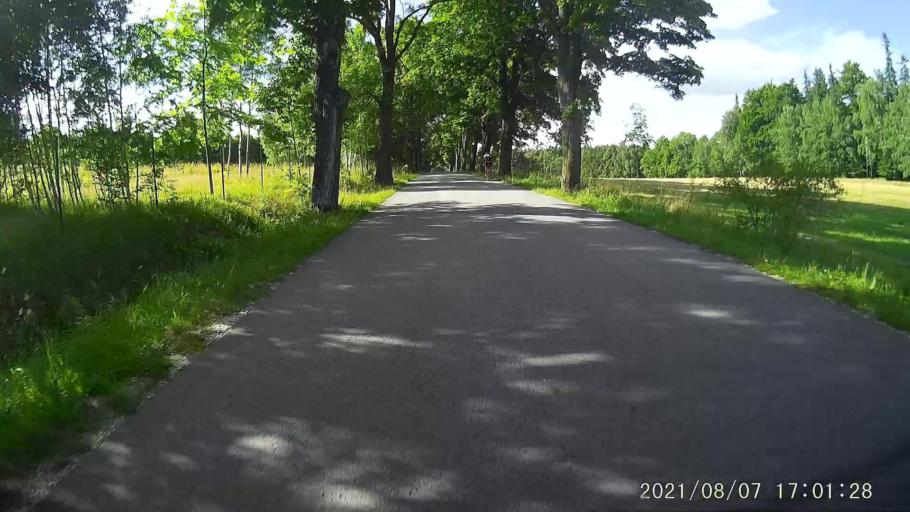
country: PL
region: Lower Silesian Voivodeship
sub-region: Powiat klodzki
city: Bystrzyca Klodzka
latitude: 50.2868
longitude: 16.5544
